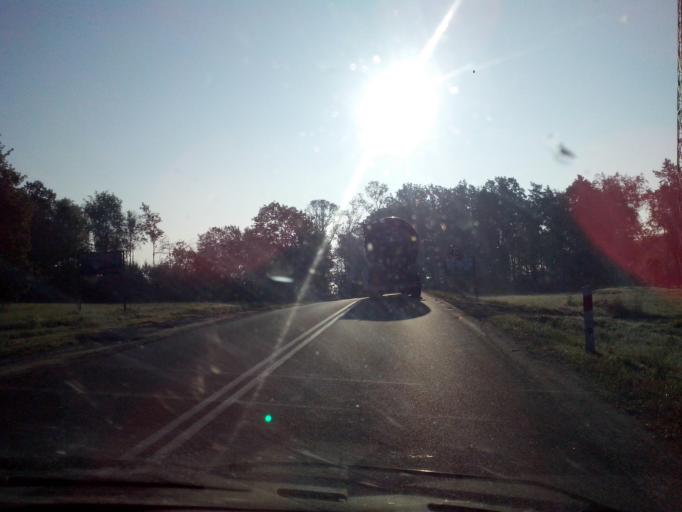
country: PL
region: Subcarpathian Voivodeship
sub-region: Powiat przemyski
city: Krasiczyn
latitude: 49.7881
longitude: 22.6074
